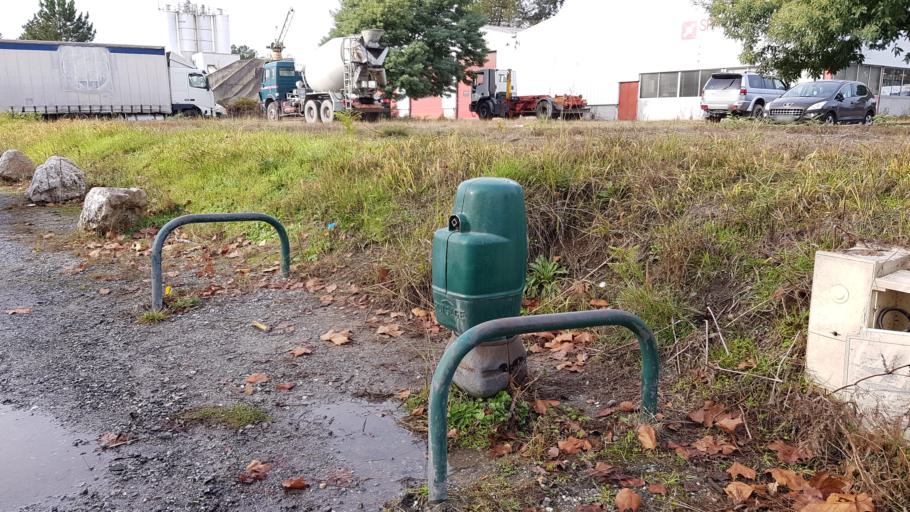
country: FR
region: Aquitaine
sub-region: Departement des Landes
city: Saint-Paul-les-Dax
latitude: 43.7572
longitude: -1.0628
